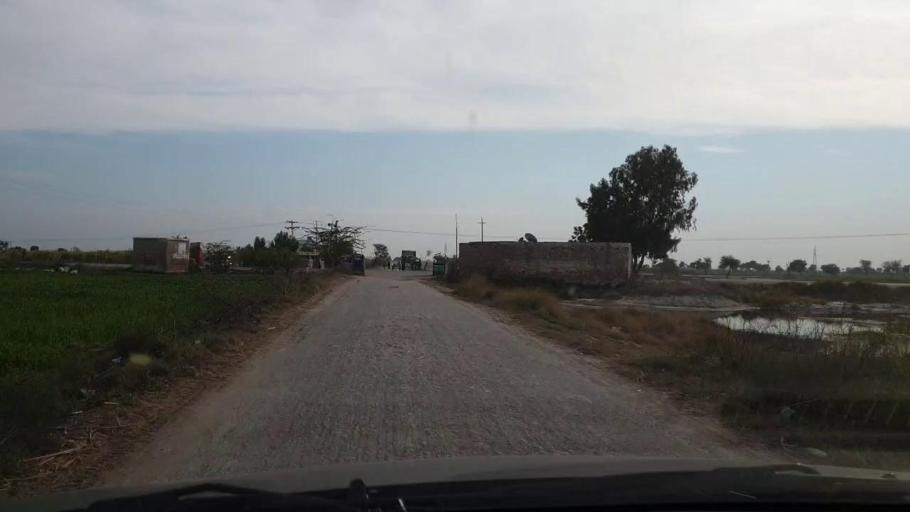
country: PK
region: Sindh
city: Khadro
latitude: 26.1193
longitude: 68.7961
